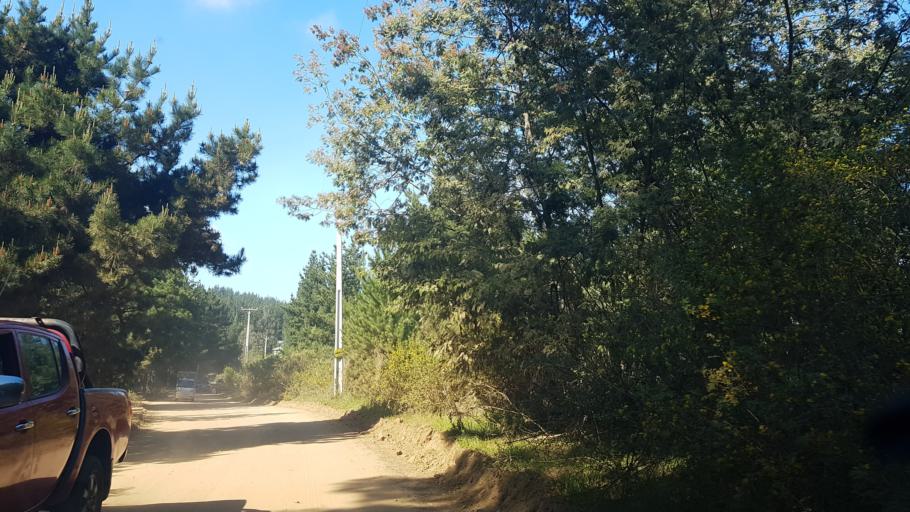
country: CL
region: Valparaiso
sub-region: Provincia de Valparaiso
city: Valparaiso
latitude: -33.1271
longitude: -71.6675
